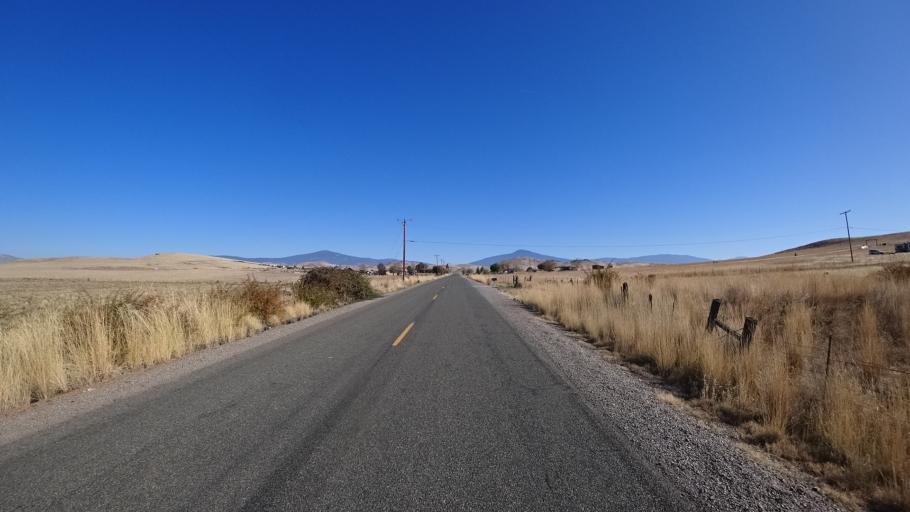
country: US
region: California
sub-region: Siskiyou County
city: Montague
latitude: 41.7558
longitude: -122.4698
